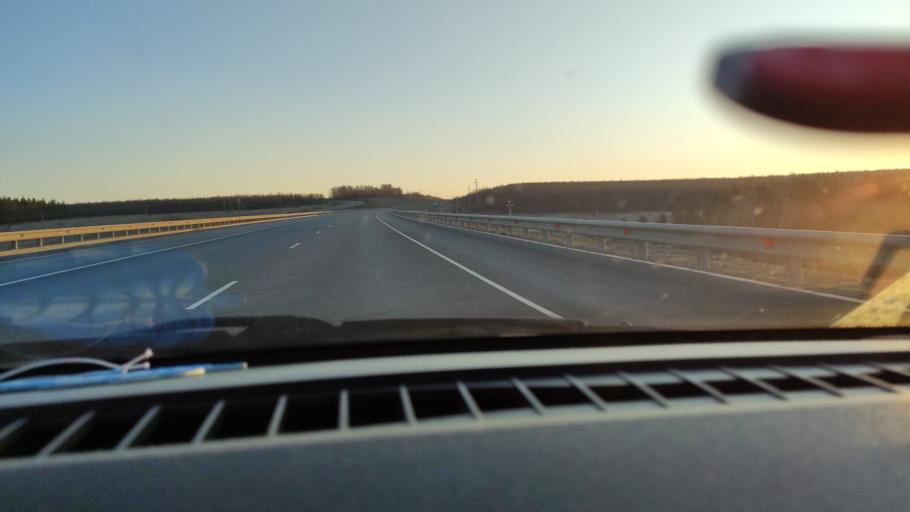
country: RU
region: Saratov
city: Yelshanka
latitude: 51.8795
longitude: 46.5096
